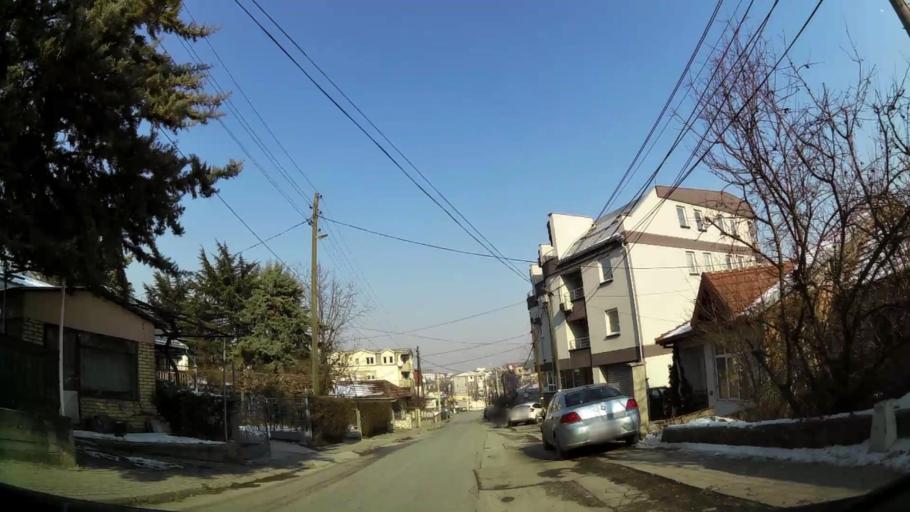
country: MK
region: Sopiste
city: Sopishte
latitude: 41.9745
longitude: 21.4382
